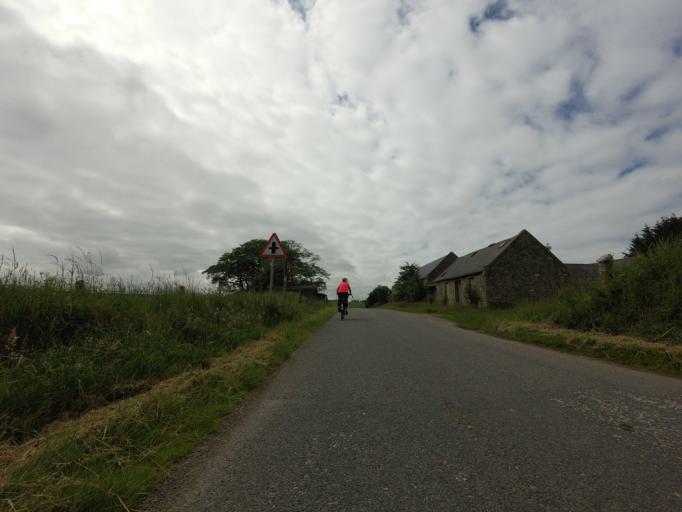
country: GB
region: Scotland
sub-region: Aberdeenshire
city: Turriff
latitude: 57.5426
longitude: -2.2725
